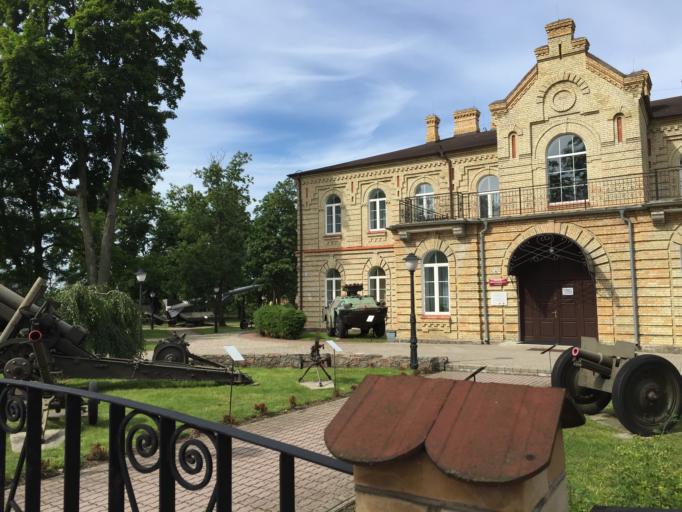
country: PL
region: Podlasie
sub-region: Suwalki
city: Suwalki
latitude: 54.0852
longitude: 22.9299
